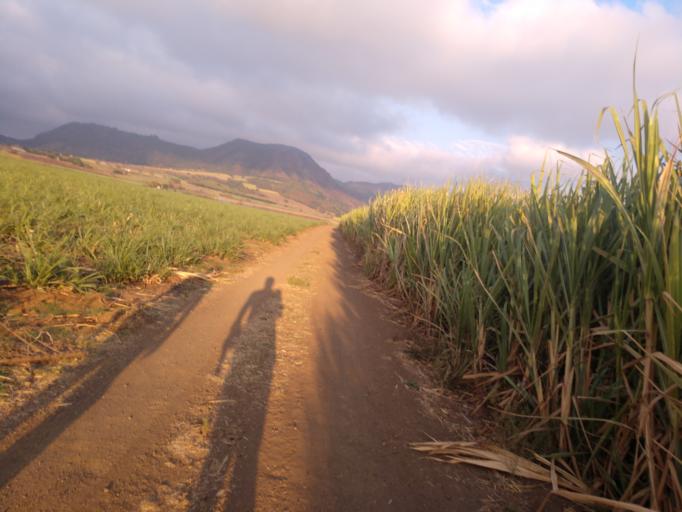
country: MX
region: Nayarit
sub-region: Tepic
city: La Corregidora
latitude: 21.4851
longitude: -104.8084
